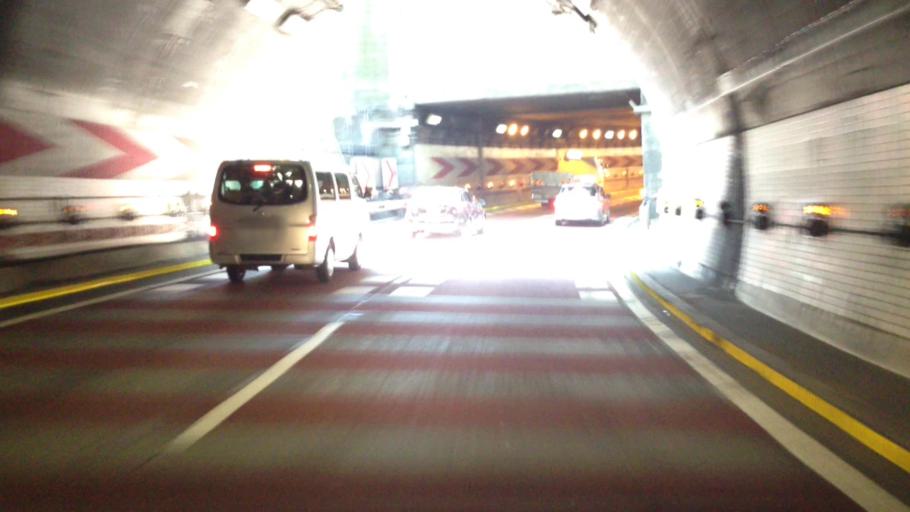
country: JP
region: Kanagawa
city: Yokohama
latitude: 35.4720
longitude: 139.5948
